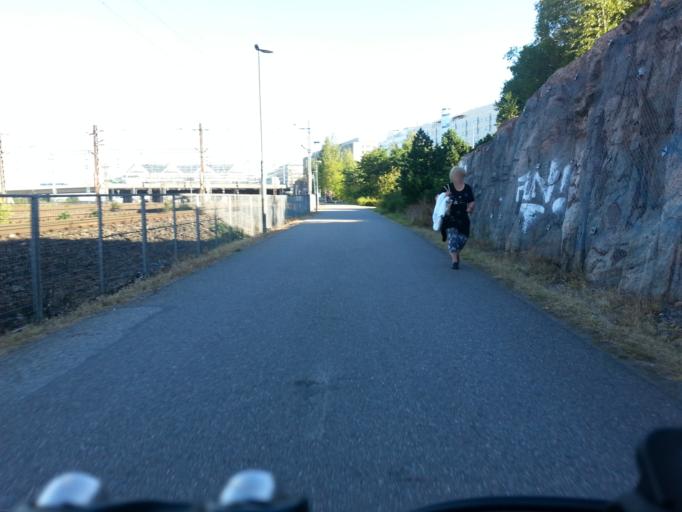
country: FI
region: Uusimaa
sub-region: Helsinki
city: Helsinki
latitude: 60.1952
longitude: 24.9346
